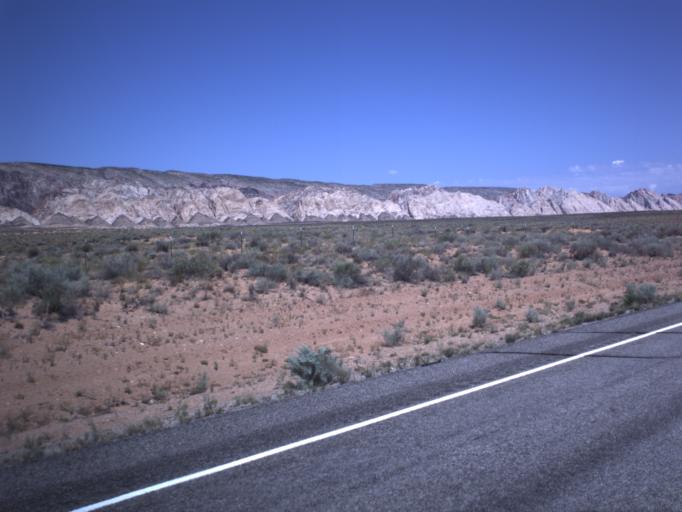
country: US
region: Utah
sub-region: Emery County
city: Castle Dale
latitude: 38.7882
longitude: -110.4380
